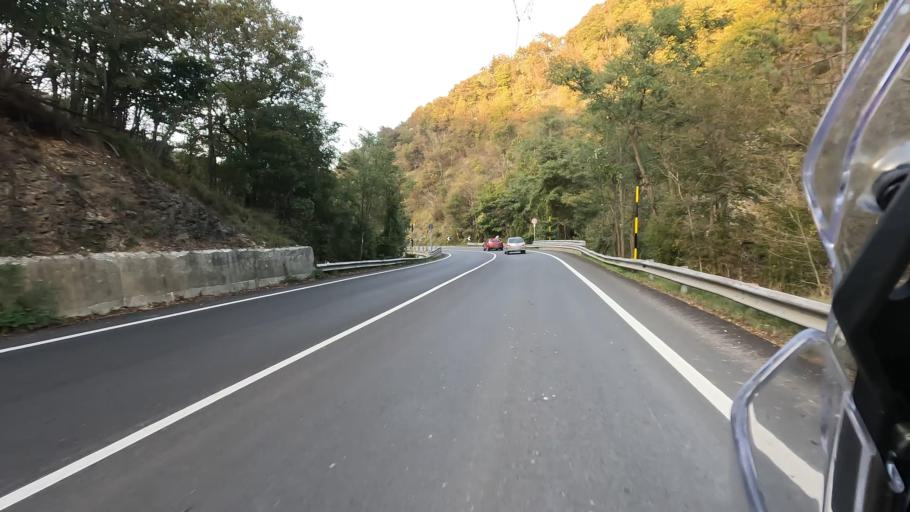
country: IT
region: Liguria
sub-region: Provincia di Savona
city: Osteria dei Cacciatori-Stella
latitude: 44.4510
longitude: 8.4785
